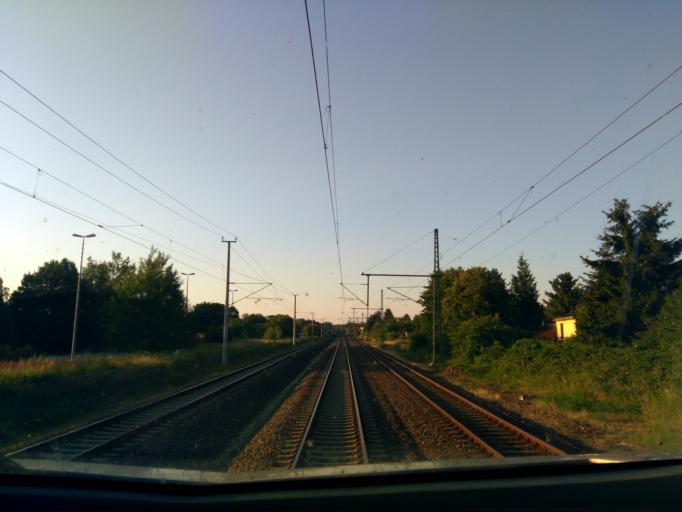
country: DE
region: Brandenburg
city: Halbe
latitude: 52.1118
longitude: 13.6982
